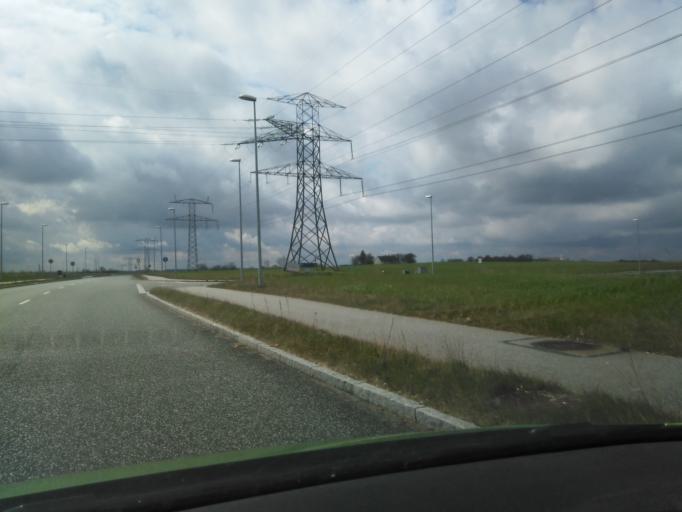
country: DK
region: Central Jutland
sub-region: Arhus Kommune
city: Framlev
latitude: 56.1563
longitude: 10.0594
